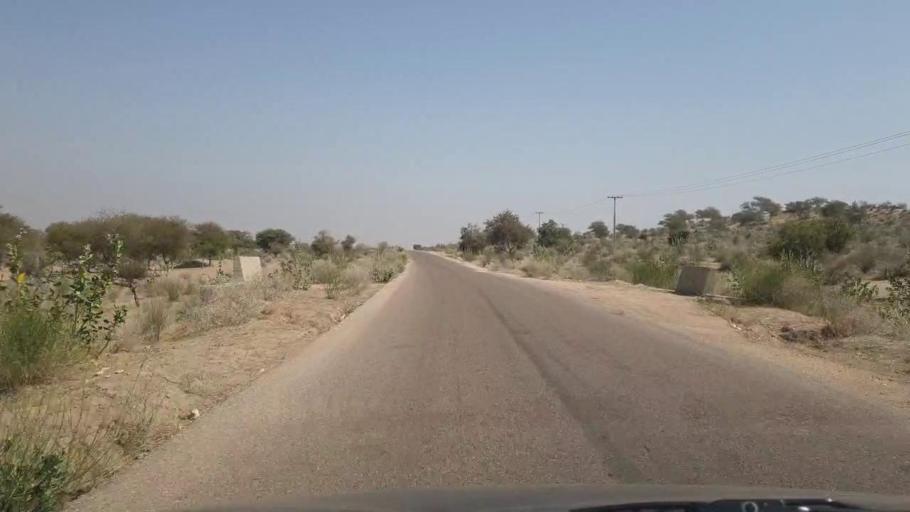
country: PK
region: Sindh
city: Chor
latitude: 25.6360
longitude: 70.0781
